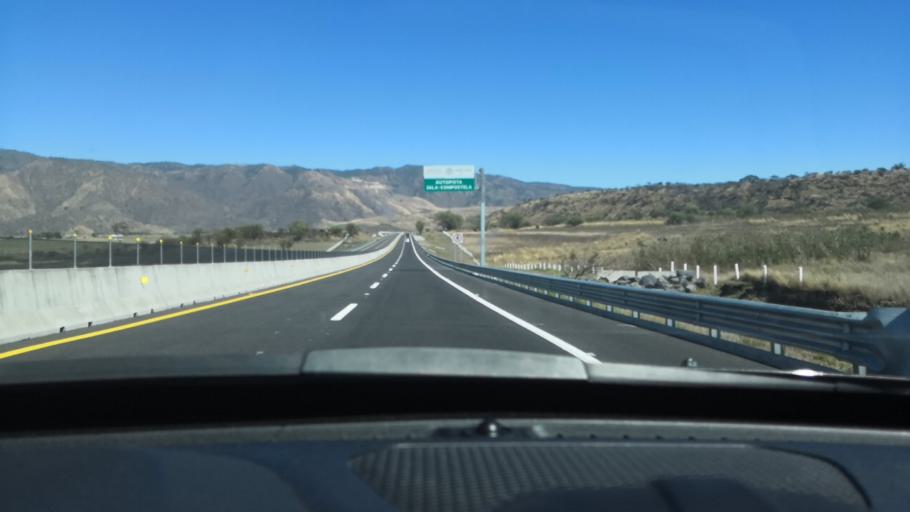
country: MX
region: Nayarit
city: Jala
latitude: 21.0754
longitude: -104.4485
